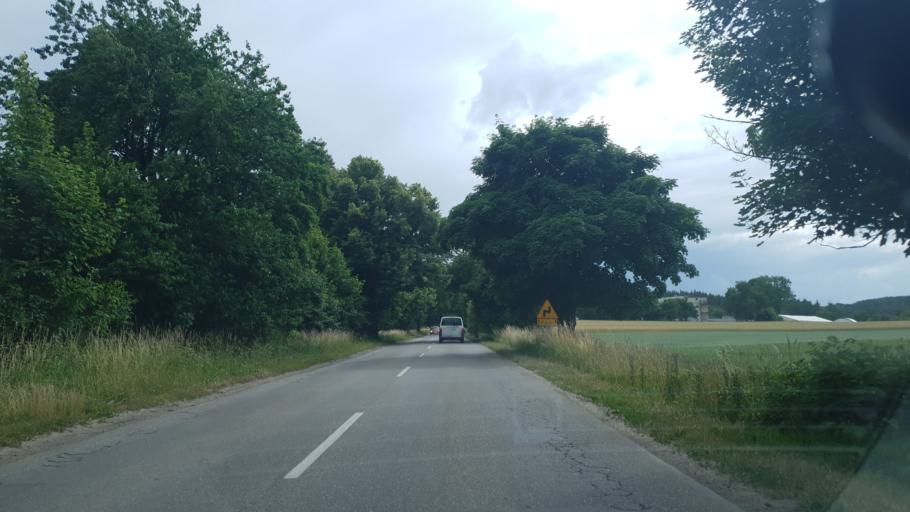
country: PL
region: Pomeranian Voivodeship
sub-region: Powiat kartuski
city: Przodkowo
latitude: 54.3721
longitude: 18.2810
